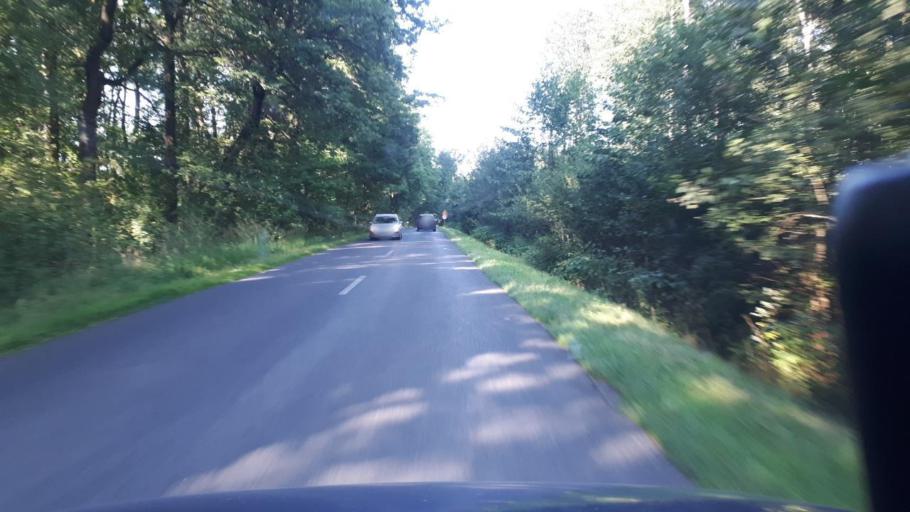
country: PL
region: Silesian Voivodeship
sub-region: Powiat tarnogorski
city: Tworog
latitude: 50.4796
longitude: 18.6864
